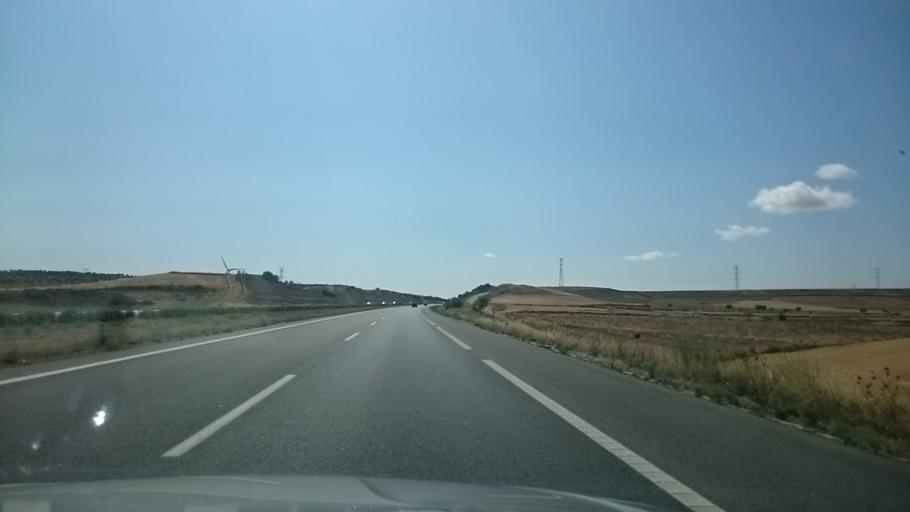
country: ES
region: Aragon
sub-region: Provincia de Zaragoza
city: Mallen
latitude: 41.8851
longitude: -1.4131
